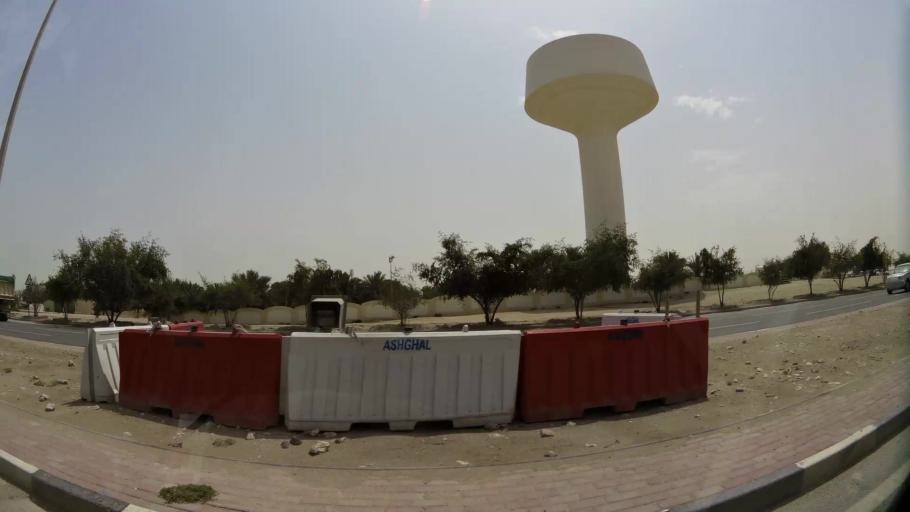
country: QA
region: Baladiyat ar Rayyan
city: Ar Rayyan
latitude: 25.2440
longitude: 51.4167
